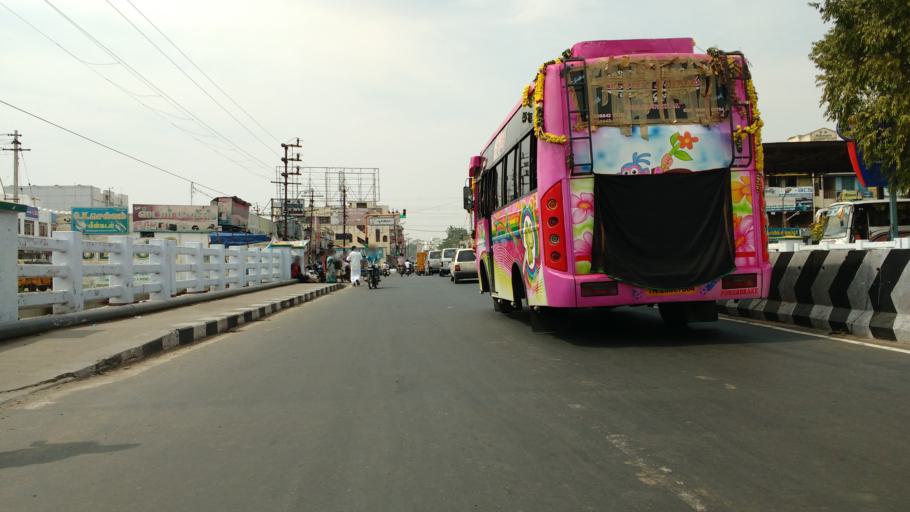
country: IN
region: Tamil Nadu
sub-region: Erode
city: Gobichettipalayam
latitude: 11.4549
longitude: 77.4363
